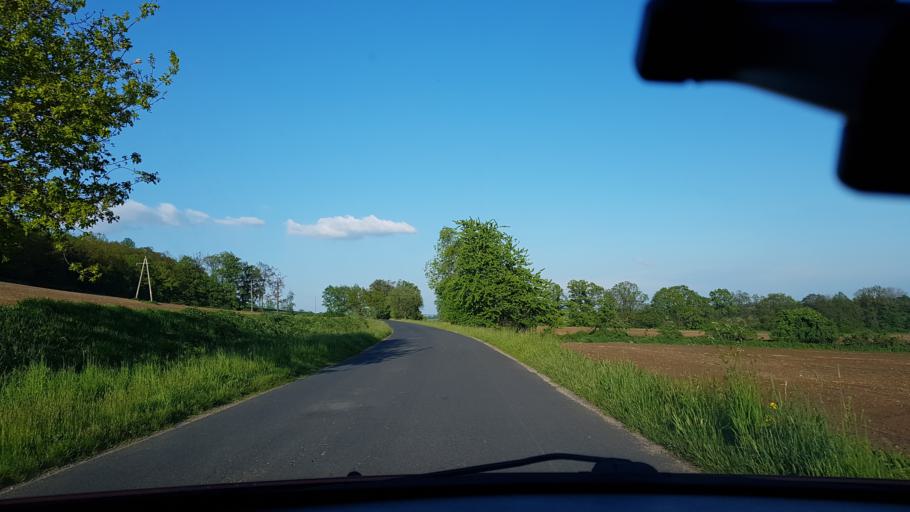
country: PL
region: Lower Silesian Voivodeship
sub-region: Powiat zabkowicki
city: Budzow
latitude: 50.6129
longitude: 16.6856
